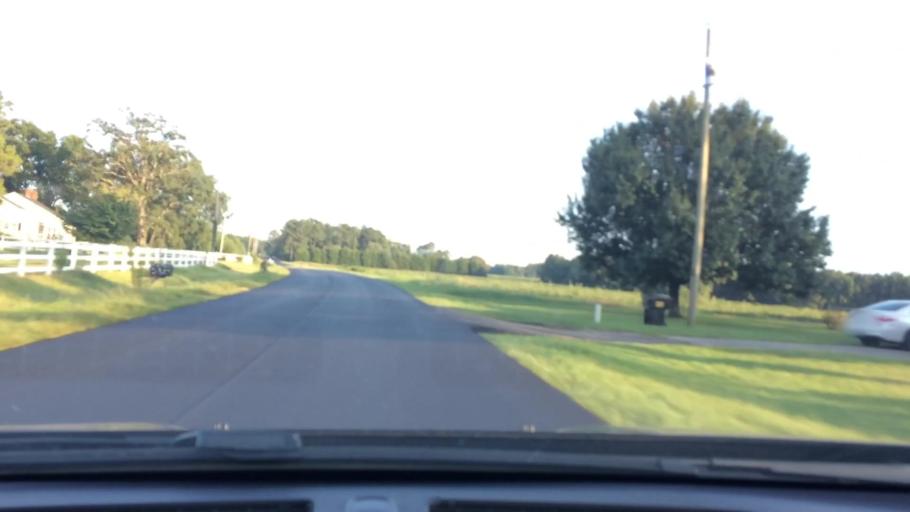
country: US
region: North Carolina
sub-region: Pitt County
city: Ayden
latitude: 35.4535
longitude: -77.4674
